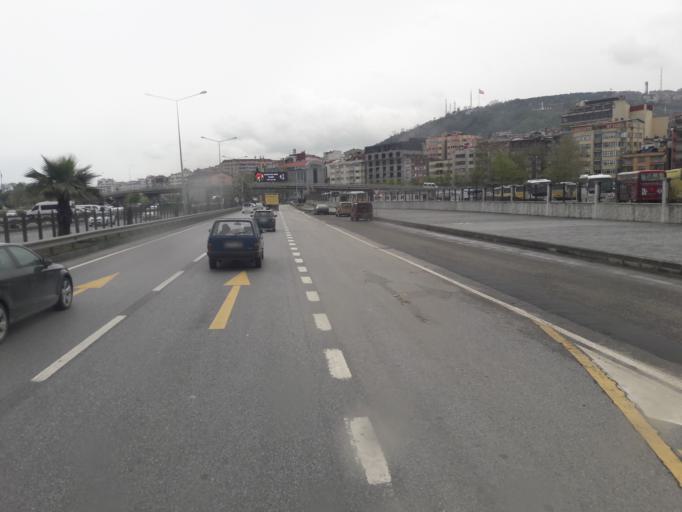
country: TR
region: Trabzon
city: Trabzon
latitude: 41.0103
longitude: 39.7248
